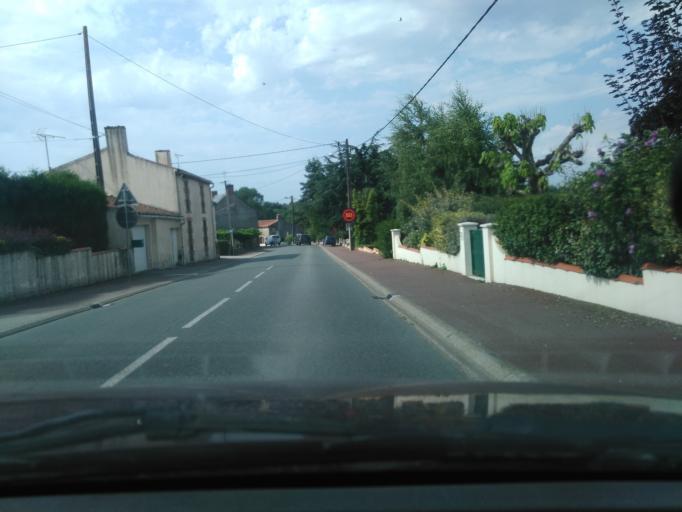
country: FR
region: Pays de la Loire
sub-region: Departement de la Vendee
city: Dompierre-sur-Yon
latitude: 46.7355
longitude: -1.3807
